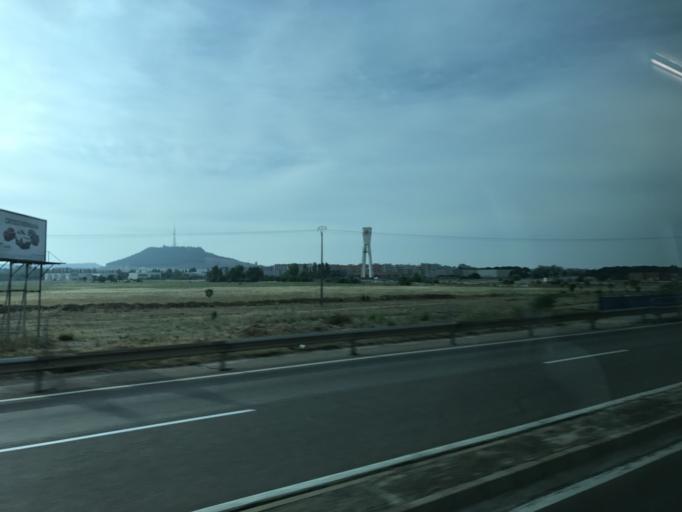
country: ES
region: Castille and Leon
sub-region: Provincia de Valladolid
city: Valladolid
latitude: 41.6238
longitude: -4.7260
